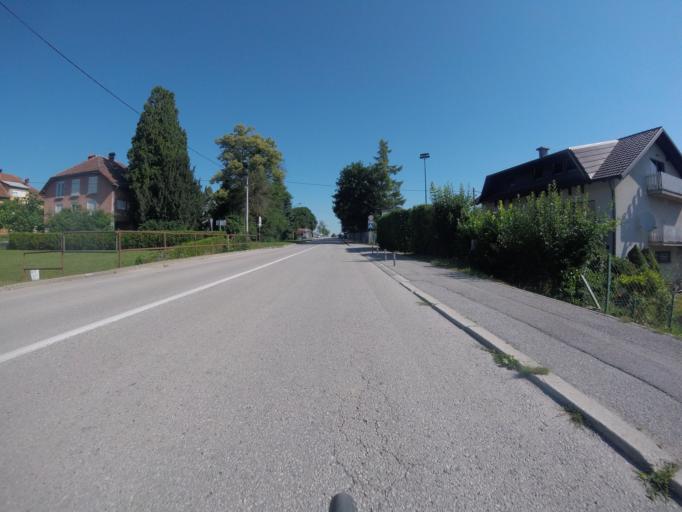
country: HR
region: Zagrebacka
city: Bregana
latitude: 45.8369
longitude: 15.6882
